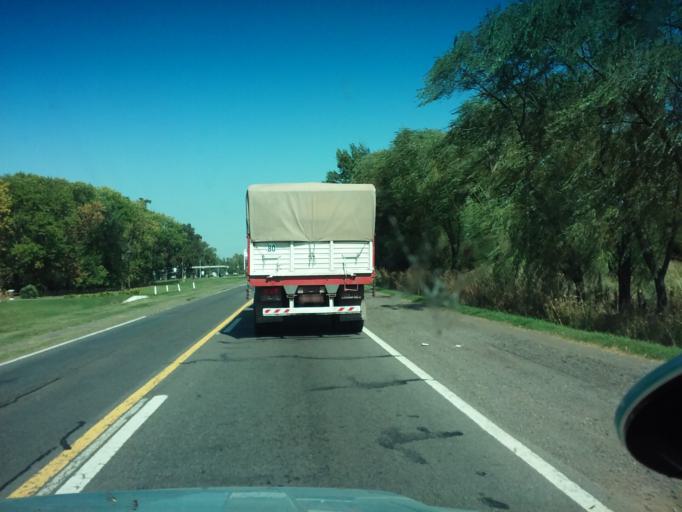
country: AR
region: Buenos Aires
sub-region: Partido de Alberti
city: Alberti
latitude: -35.0553
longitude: -60.2677
